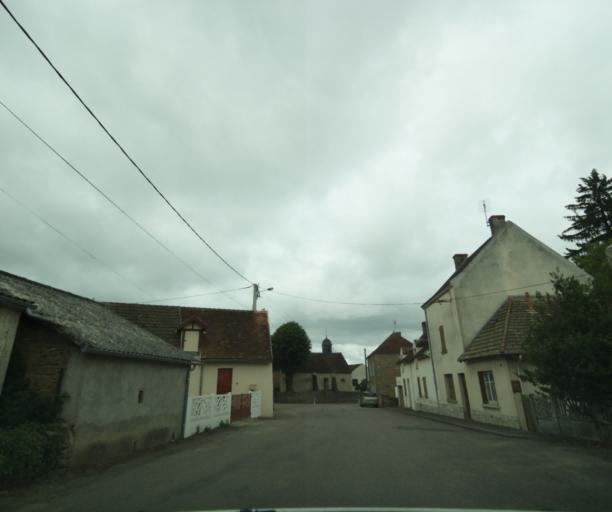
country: FR
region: Bourgogne
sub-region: Departement de Saone-et-Loire
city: Charolles
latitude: 46.4327
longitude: 4.2696
